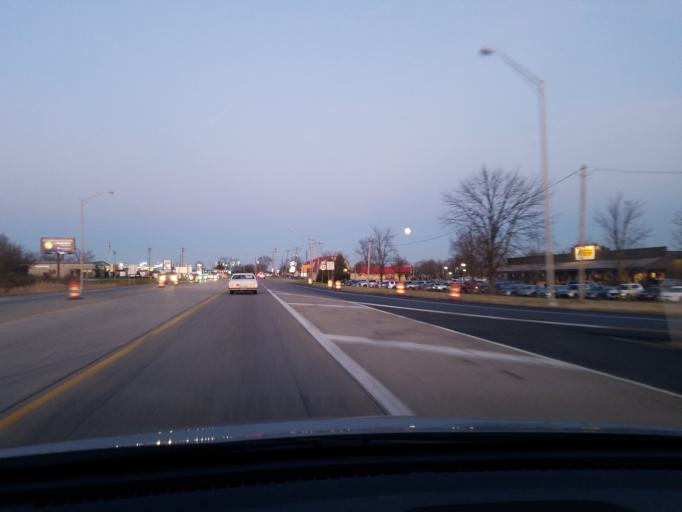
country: US
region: Indiana
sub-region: Clark County
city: Sellersburg
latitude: 38.3948
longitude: -85.7609
